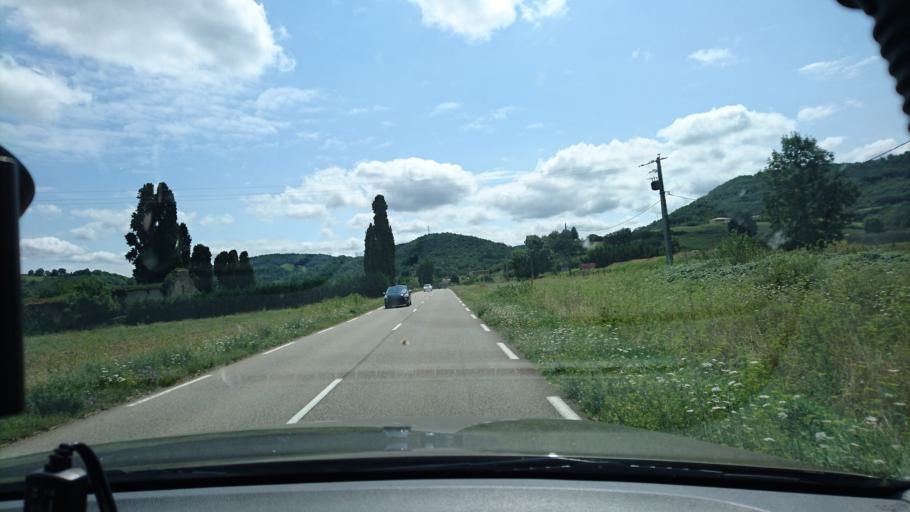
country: FR
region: Midi-Pyrenees
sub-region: Departement de la Haute-Garonne
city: Gaillac-Toulza
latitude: 43.1105
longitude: 1.4404
